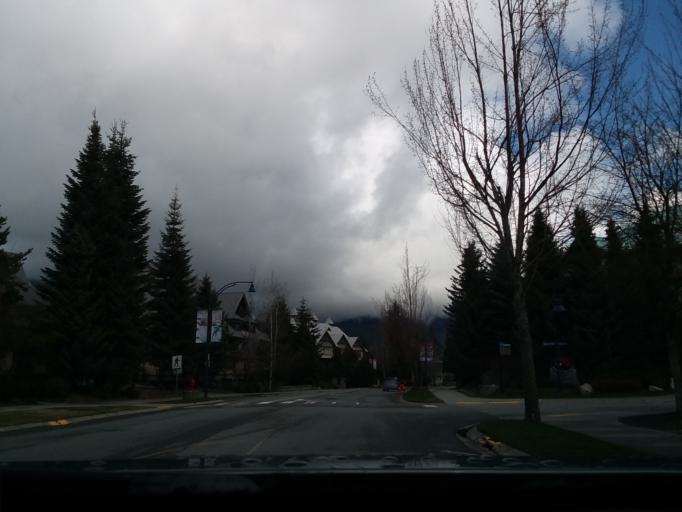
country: CA
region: British Columbia
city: Whistler
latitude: 50.1181
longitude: -122.9583
